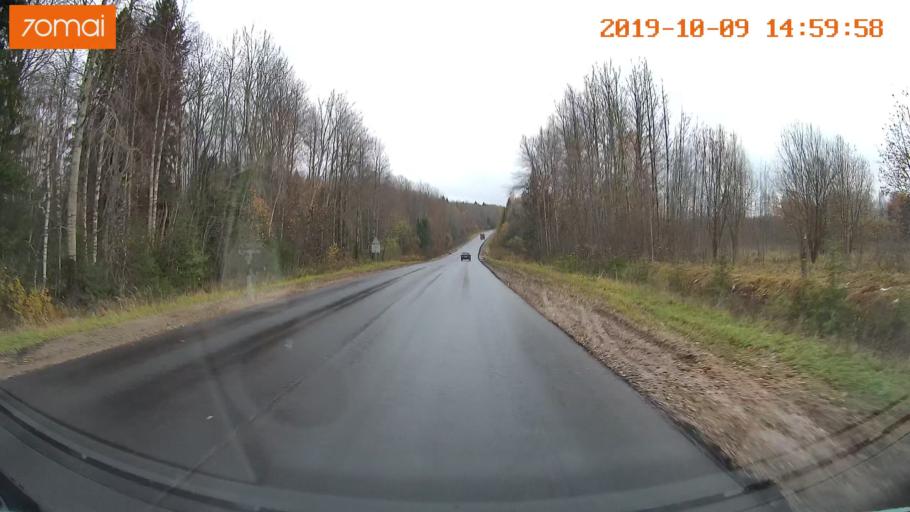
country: RU
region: Kostroma
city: Chistyye Bory
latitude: 58.3145
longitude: 41.6742
